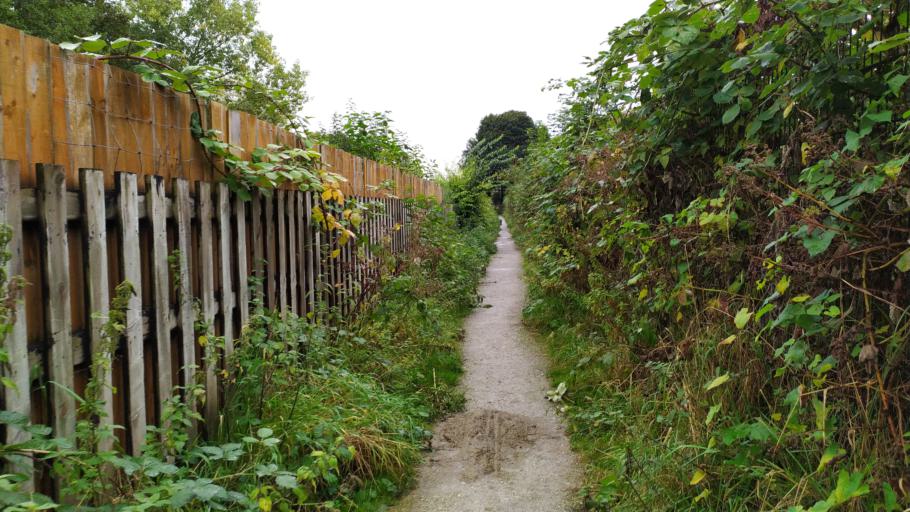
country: GB
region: England
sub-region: City and Borough of Leeds
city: Chapel Allerton
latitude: 53.8293
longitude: -1.5731
